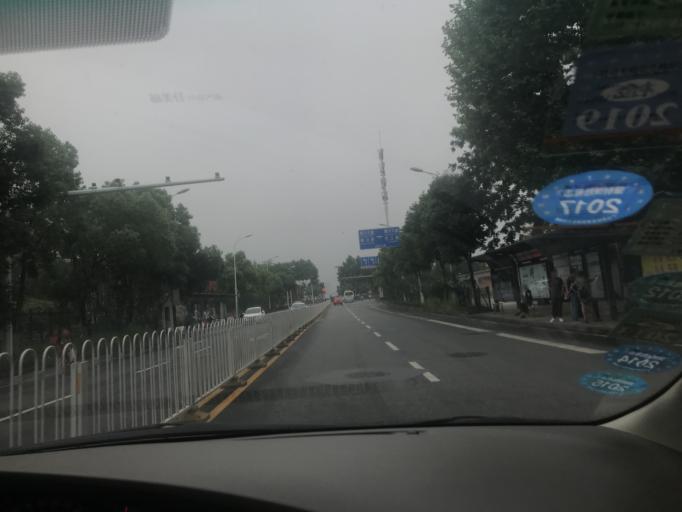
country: CN
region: Hubei
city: Wuhan
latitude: 30.5519
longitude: 114.2729
